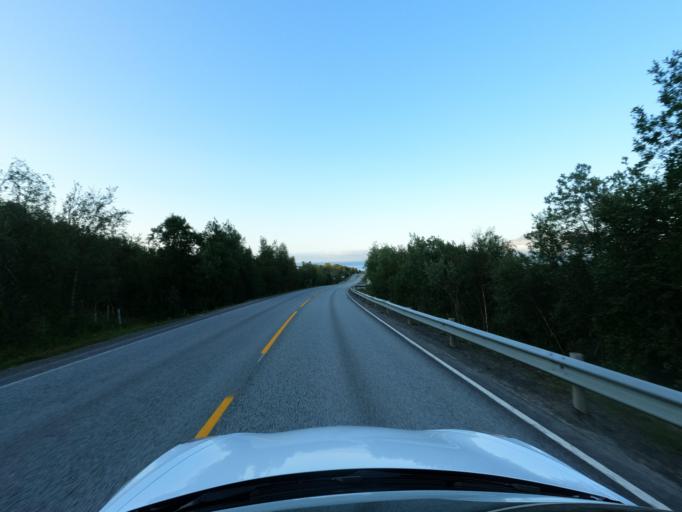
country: NO
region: Troms
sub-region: Harstad
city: Harstad
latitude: 68.7391
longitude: 16.5577
